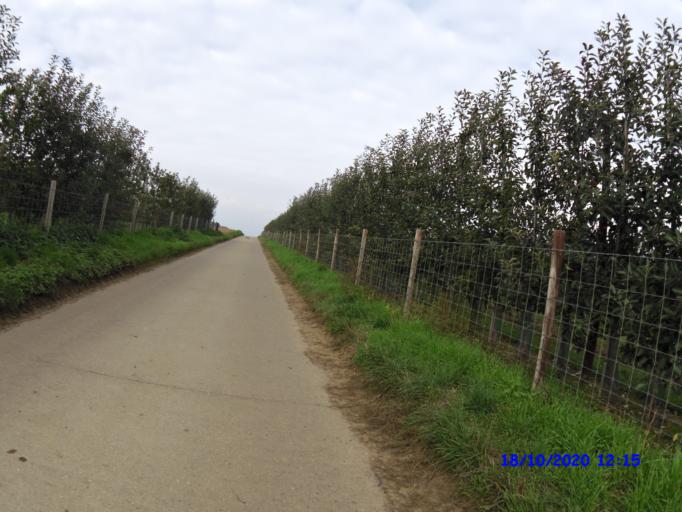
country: BE
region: Flanders
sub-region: Provincie Vlaams-Brabant
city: Landen
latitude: 50.7688
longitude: 5.0565
